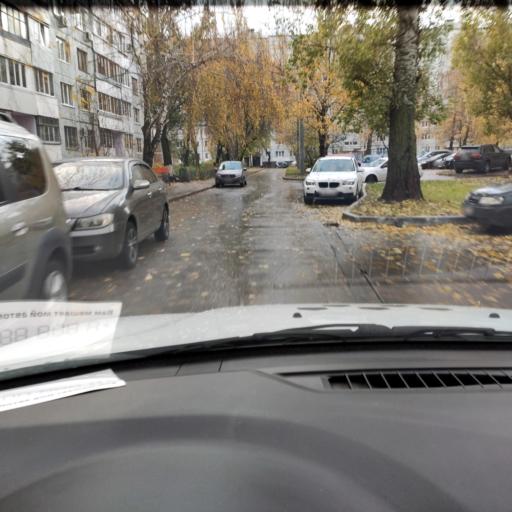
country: RU
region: Samara
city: Tol'yatti
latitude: 53.5074
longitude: 49.4372
